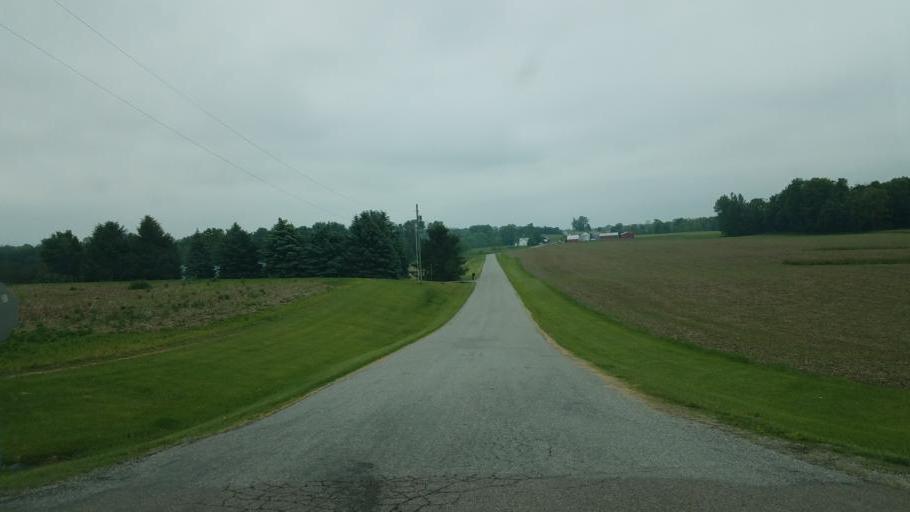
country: US
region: Ohio
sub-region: Knox County
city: Centerburg
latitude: 40.3997
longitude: -82.7318
